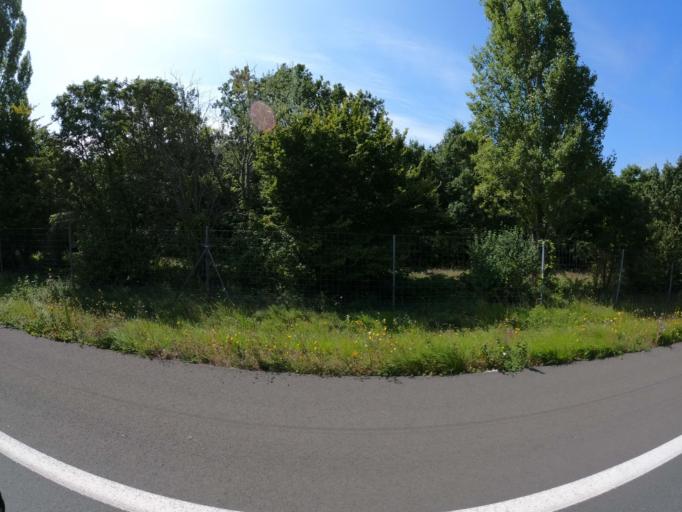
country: FR
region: Poitou-Charentes
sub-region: Departement des Deux-Sevres
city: Saint-Hilaire-la-Palud
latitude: 46.2083
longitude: -0.7362
